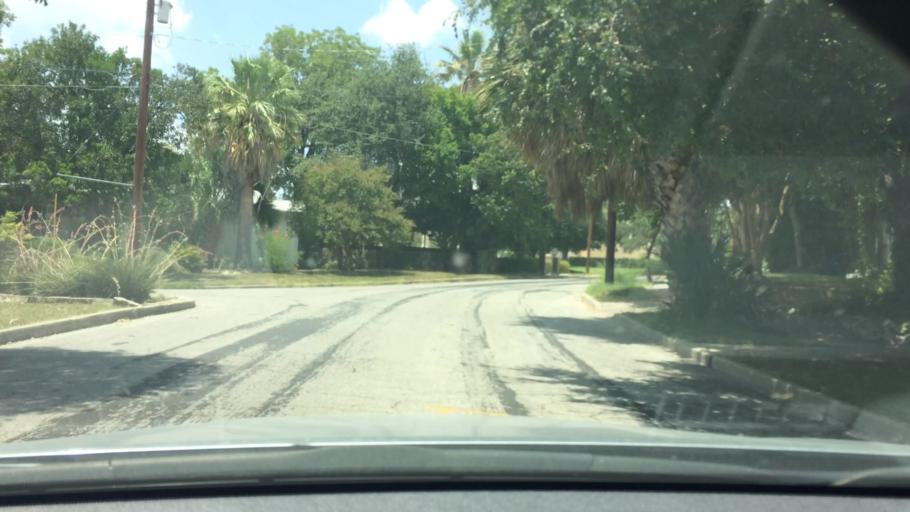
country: US
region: Texas
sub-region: Bexar County
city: Olmos Park
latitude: 29.4559
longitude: -98.4867
